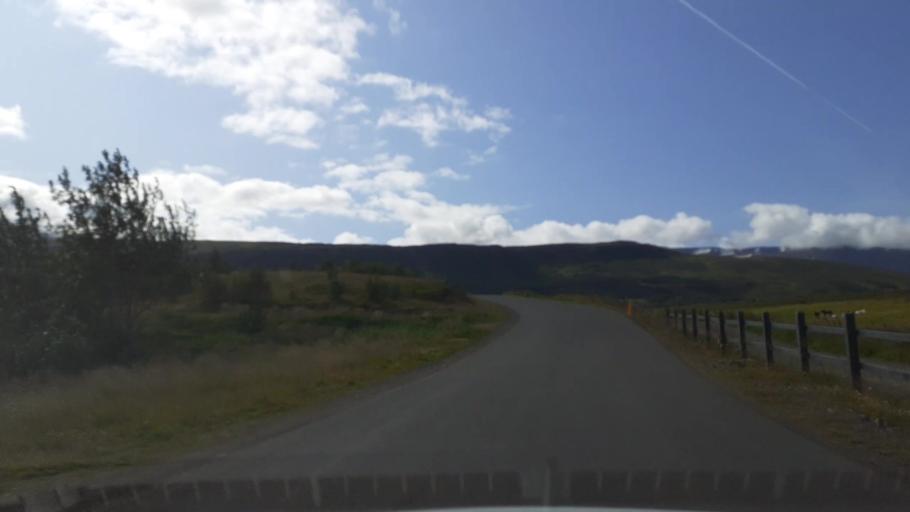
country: IS
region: Northeast
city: Akureyri
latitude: 65.6514
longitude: -18.0932
